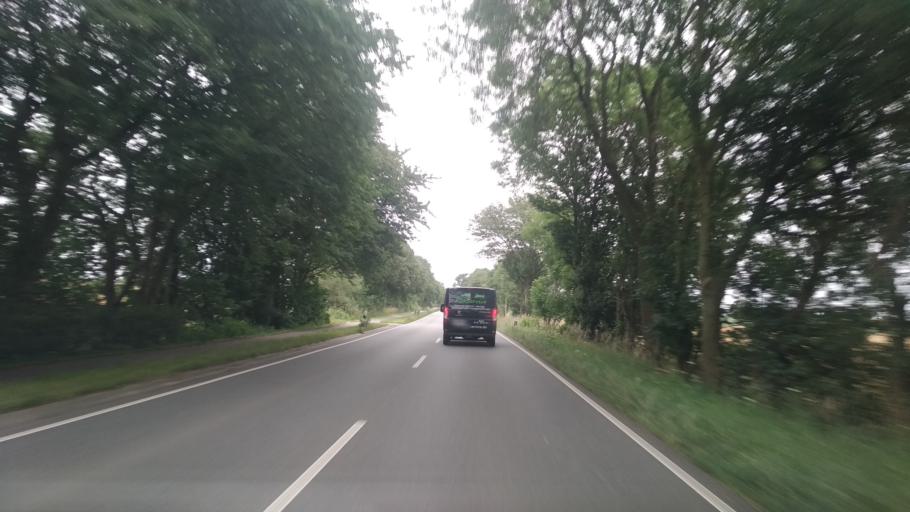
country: DE
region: Schleswig-Holstein
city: Munkbrarup
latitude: 54.8063
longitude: 9.5804
